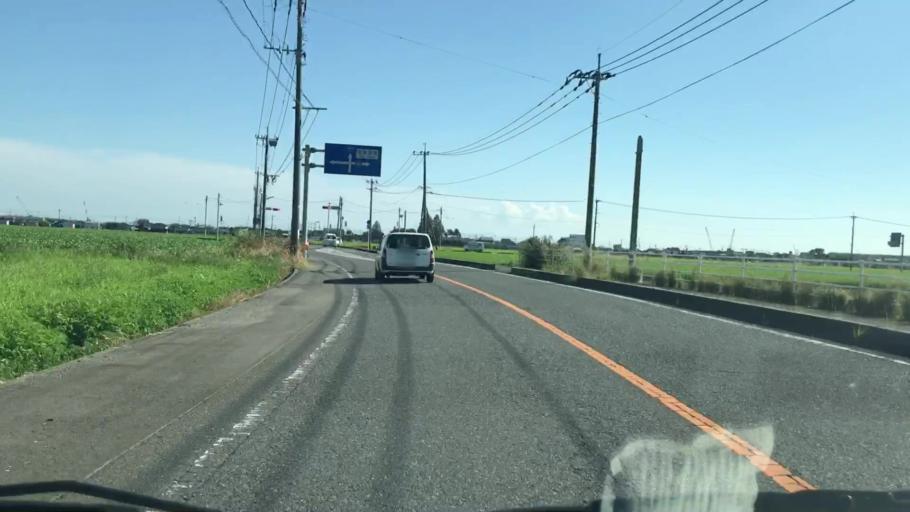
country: JP
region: Saga Prefecture
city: Okawa
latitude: 33.2218
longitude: 130.3509
